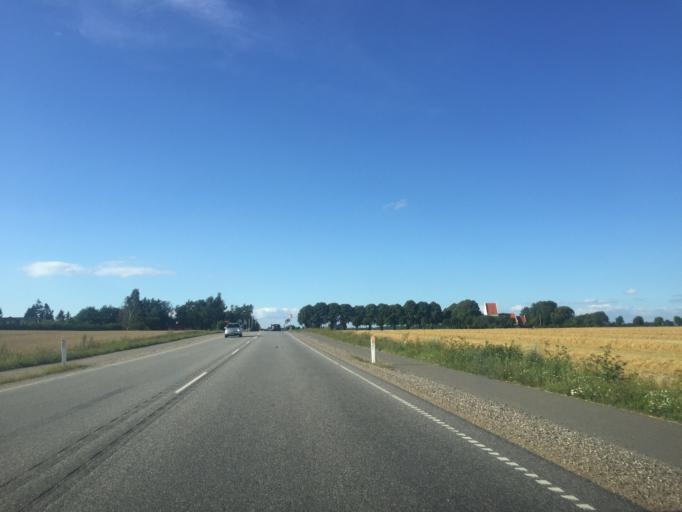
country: DK
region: Zealand
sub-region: Guldborgsund Kommune
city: Norre Alslev
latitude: 54.8449
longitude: 11.8584
